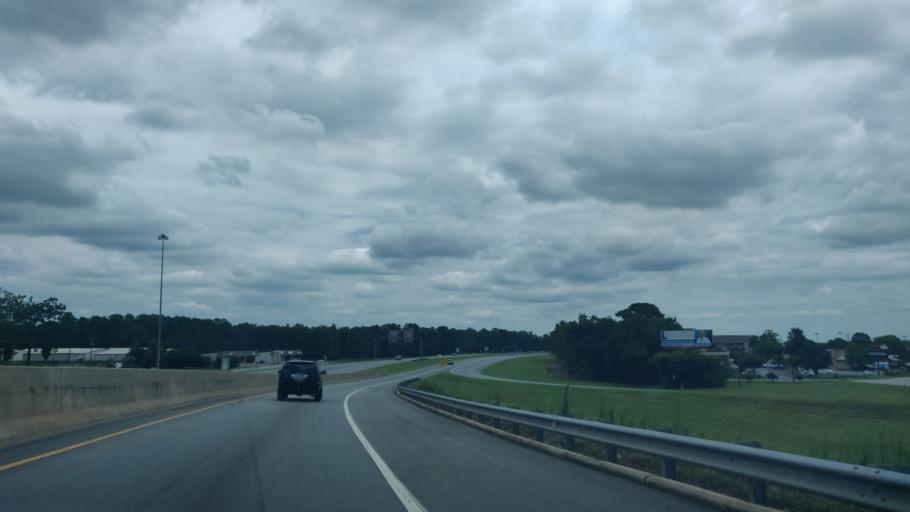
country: US
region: Georgia
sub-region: Dougherty County
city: Albany
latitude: 31.6223
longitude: -84.2297
